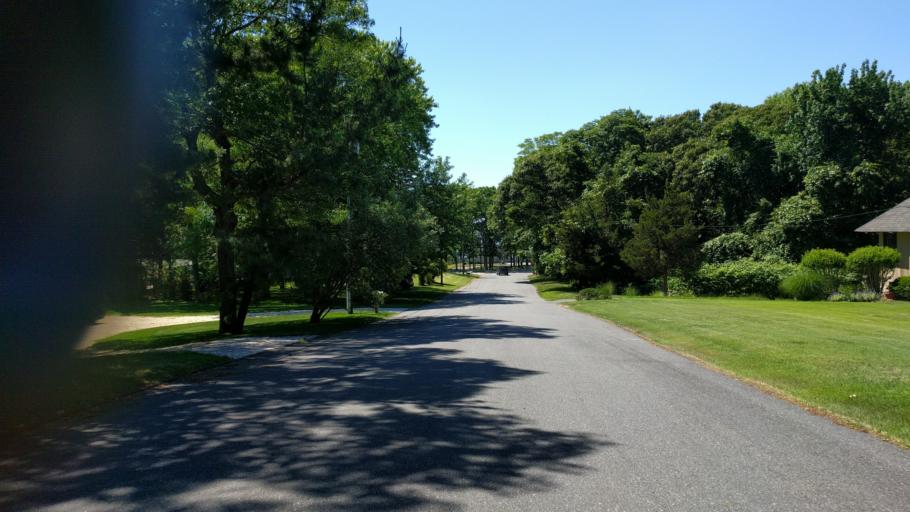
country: US
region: New York
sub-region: Suffolk County
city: Noyack
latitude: 40.9811
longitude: -72.3768
